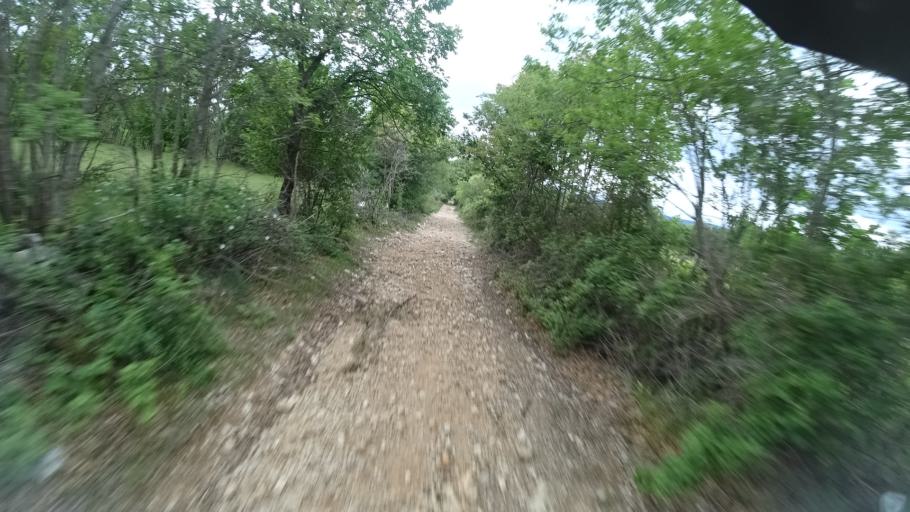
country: HR
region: Sibensko-Kniniska
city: Knin
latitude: 43.9881
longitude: 16.3164
